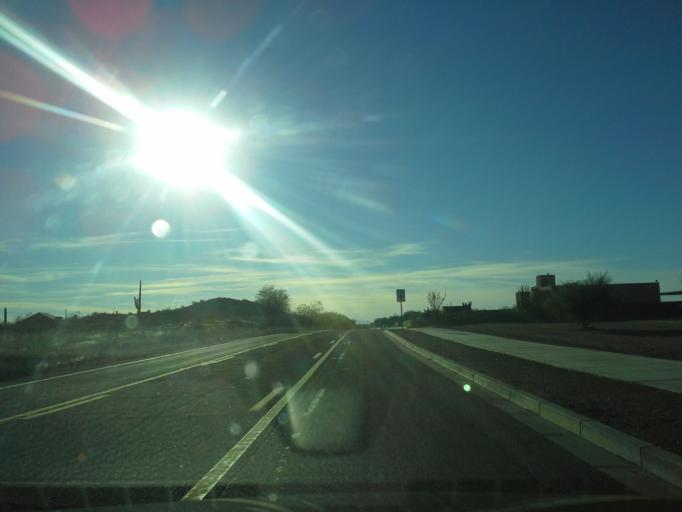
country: US
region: Arizona
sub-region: Pinal County
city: Apache Junction
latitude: 33.3607
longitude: -111.4391
